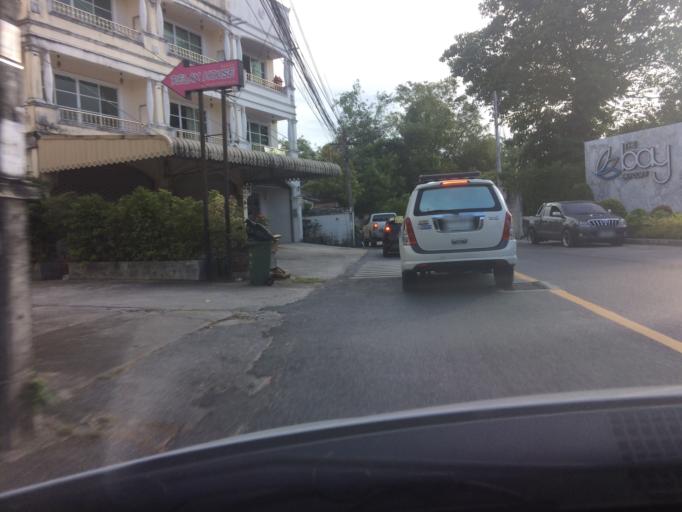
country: TH
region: Phuket
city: Ban Talat Yai
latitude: 7.8717
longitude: 98.3966
